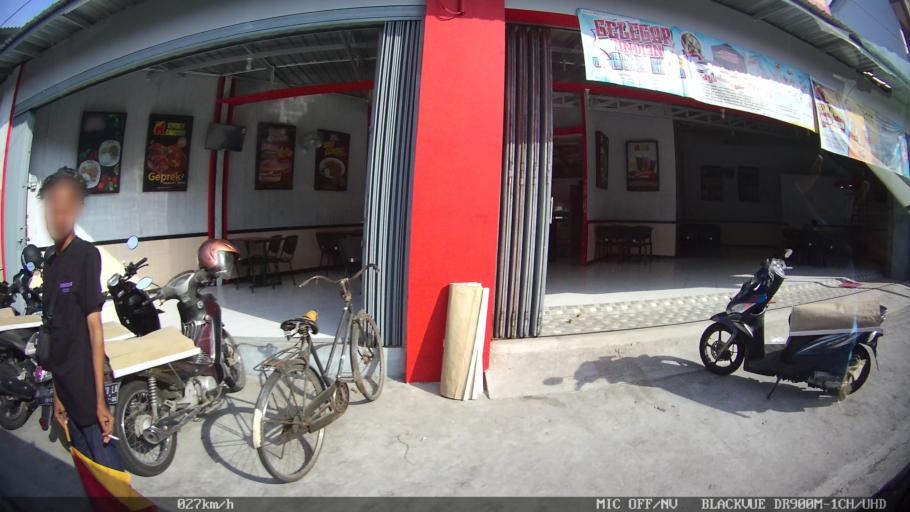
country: ID
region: Daerah Istimewa Yogyakarta
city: Bantul
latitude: -7.8811
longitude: 110.3096
